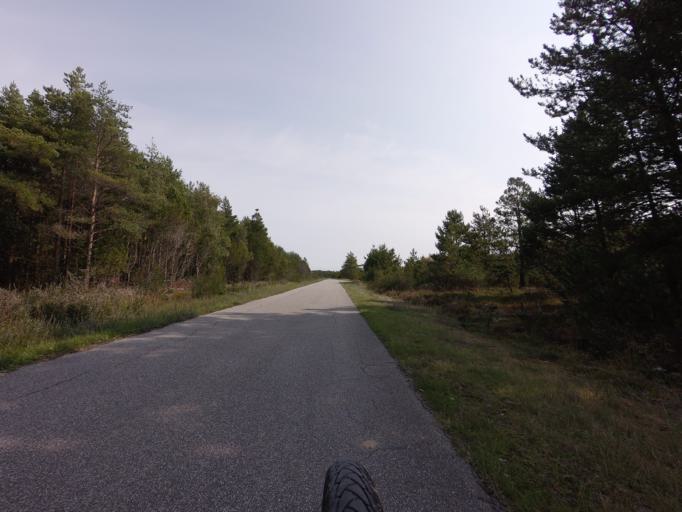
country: DK
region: North Denmark
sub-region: Frederikshavn Kommune
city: Strandby
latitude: 57.6416
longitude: 10.4233
